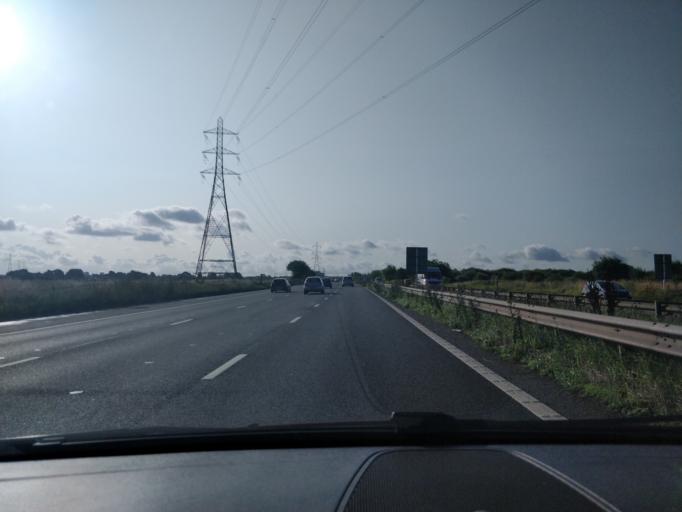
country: GB
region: England
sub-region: Sefton
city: Maghull
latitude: 53.4908
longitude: -2.9449
